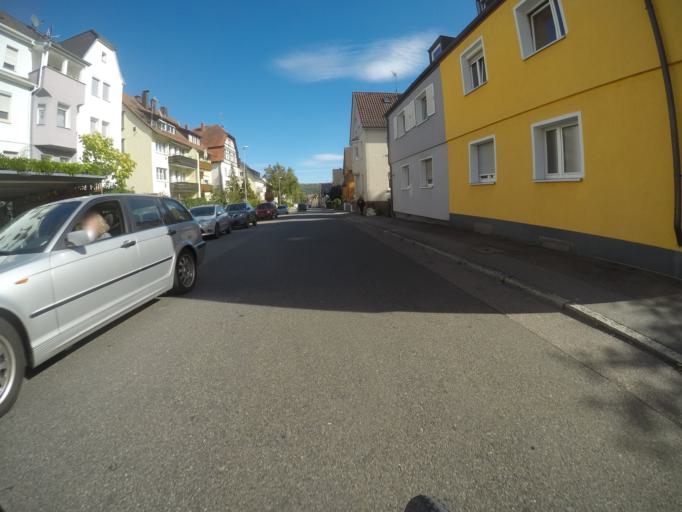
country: DE
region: Baden-Wuerttemberg
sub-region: Regierungsbezirk Stuttgart
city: Ostfildern
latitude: 48.7575
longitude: 9.2455
